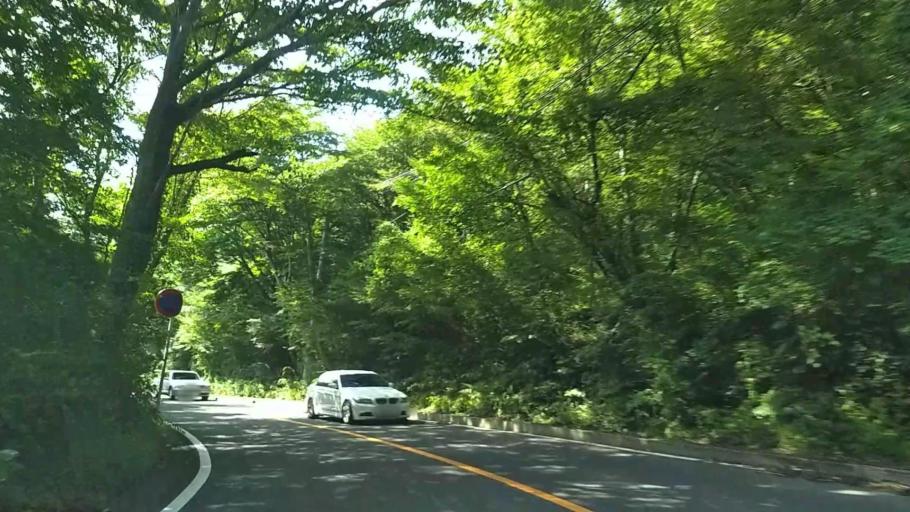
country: JP
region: Kanagawa
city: Hakone
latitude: 35.2232
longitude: 139.0064
